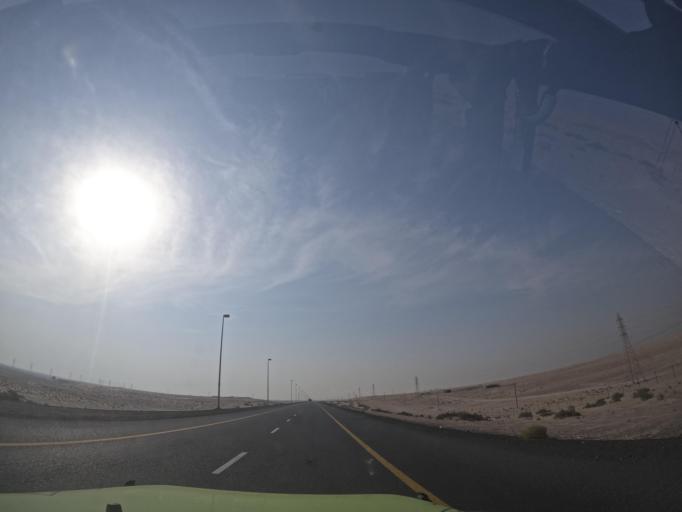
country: AE
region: Dubai
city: Dubai
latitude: 24.7518
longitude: 55.1040
